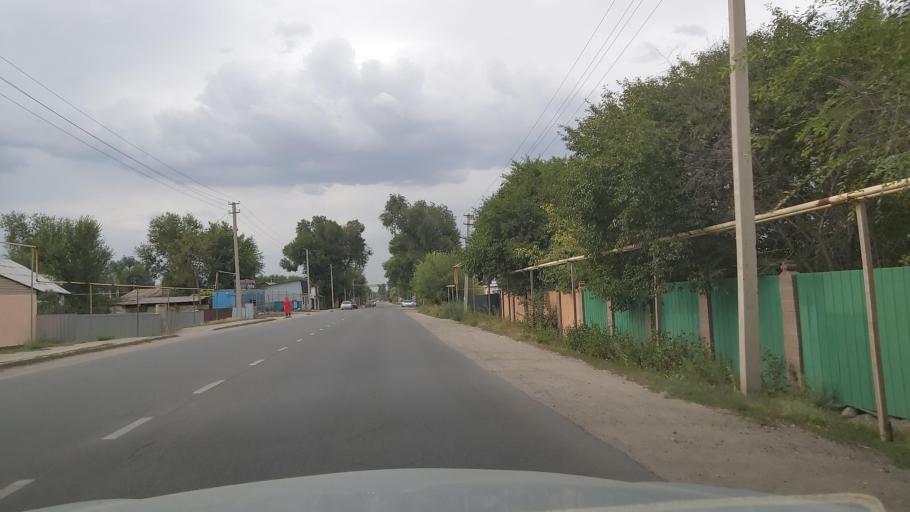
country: KZ
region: Almaty Oblysy
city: Energeticheskiy
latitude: 43.4020
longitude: 77.0642
